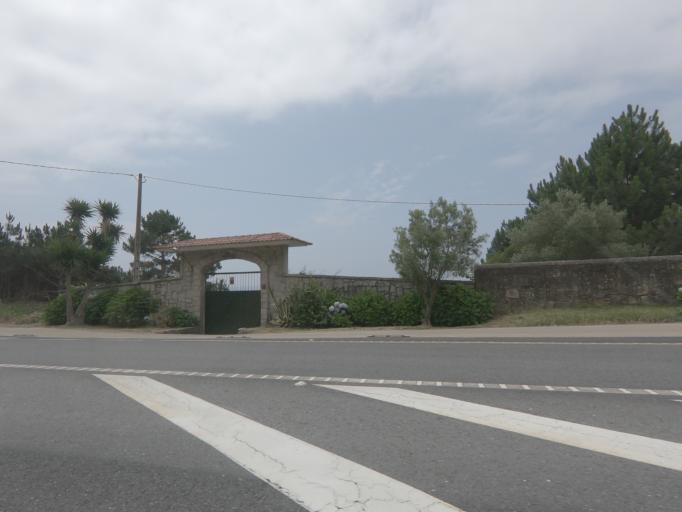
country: ES
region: Galicia
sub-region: Provincia de Pontevedra
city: Oia
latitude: 41.9728
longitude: -8.8843
